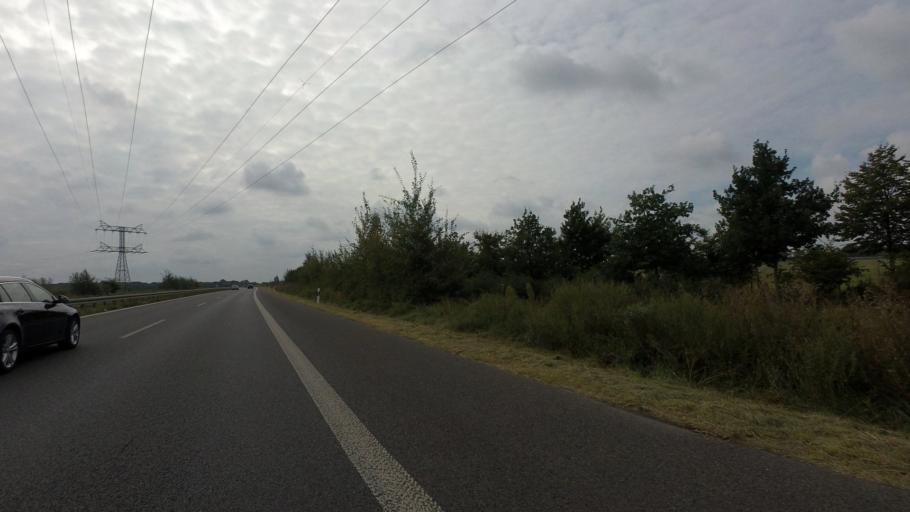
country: DE
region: Brandenburg
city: Rangsdorf
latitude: 52.3332
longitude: 13.4449
